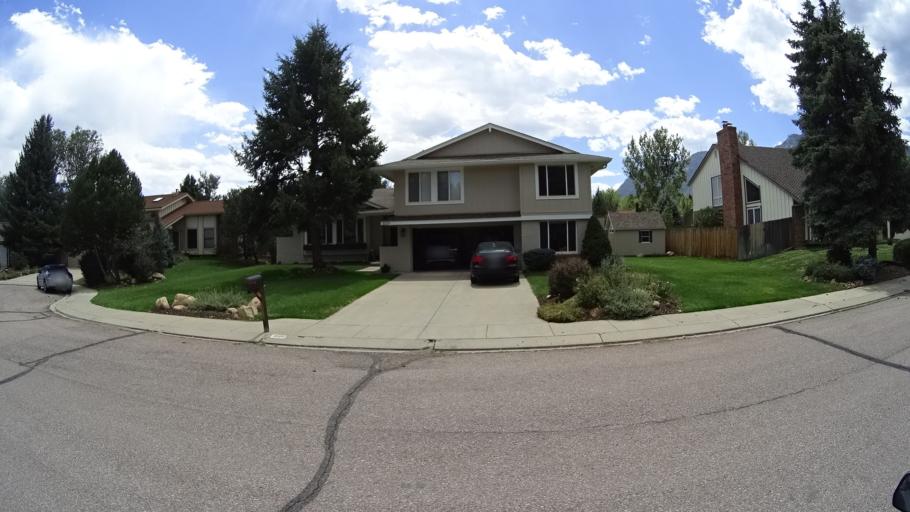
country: US
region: Colorado
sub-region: El Paso County
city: Colorado Springs
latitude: 38.7893
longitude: -104.8319
